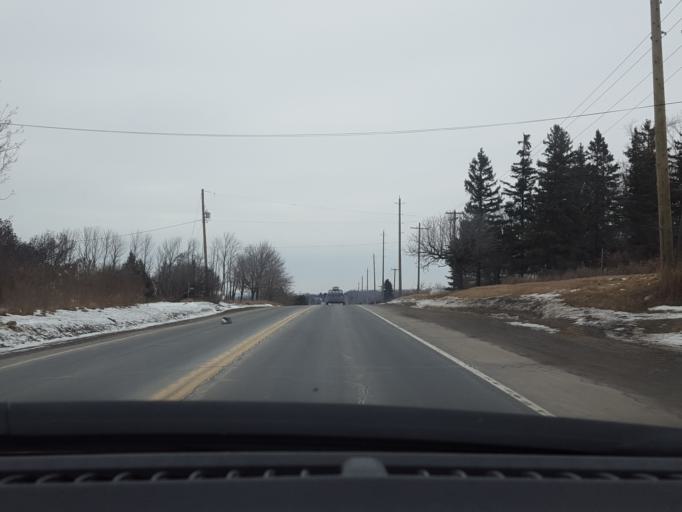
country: CA
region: Ontario
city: Newmarket
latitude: 44.1497
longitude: -79.4274
